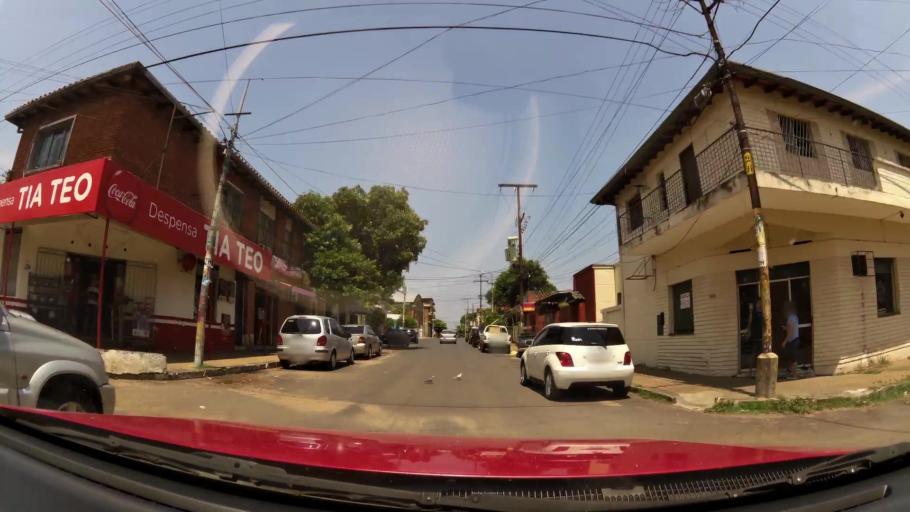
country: PY
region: Asuncion
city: Asuncion
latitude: -25.2983
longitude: -57.6453
